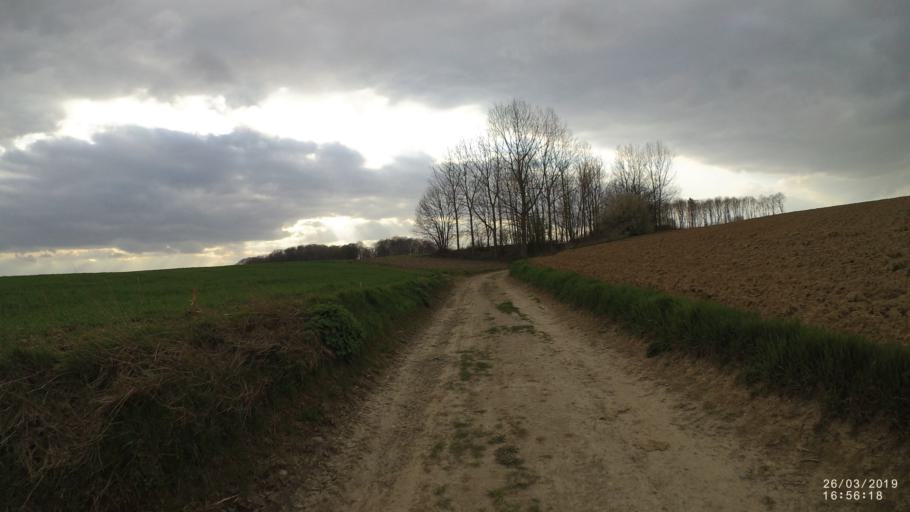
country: BE
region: Flanders
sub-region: Provincie Vlaams-Brabant
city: Bertem
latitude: 50.8411
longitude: 4.6178
